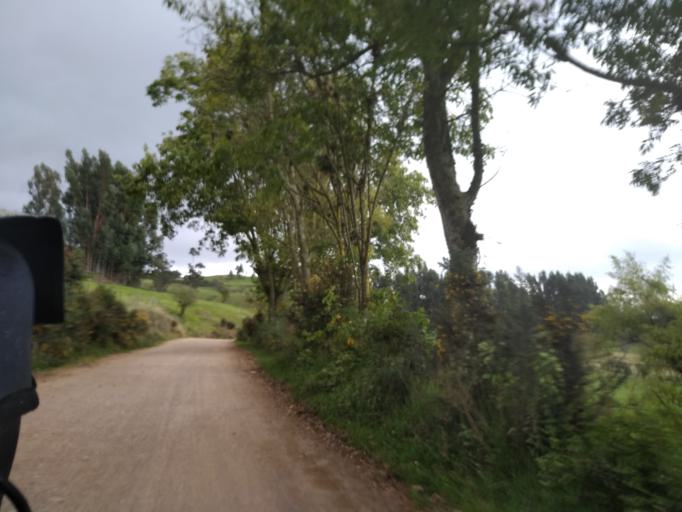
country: CO
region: Boyaca
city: Sotaquira
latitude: 5.7656
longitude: -73.2735
